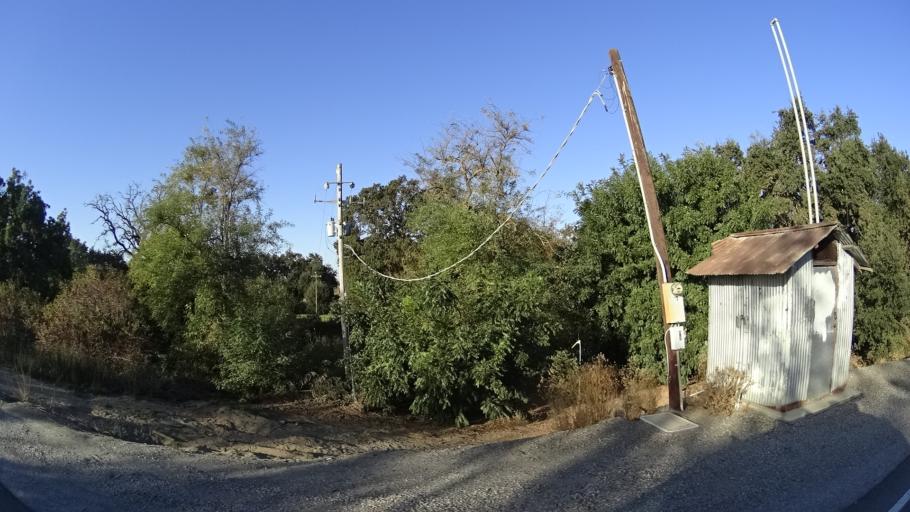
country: US
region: California
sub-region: Sacramento County
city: Parkway
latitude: 38.4291
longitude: -121.5330
